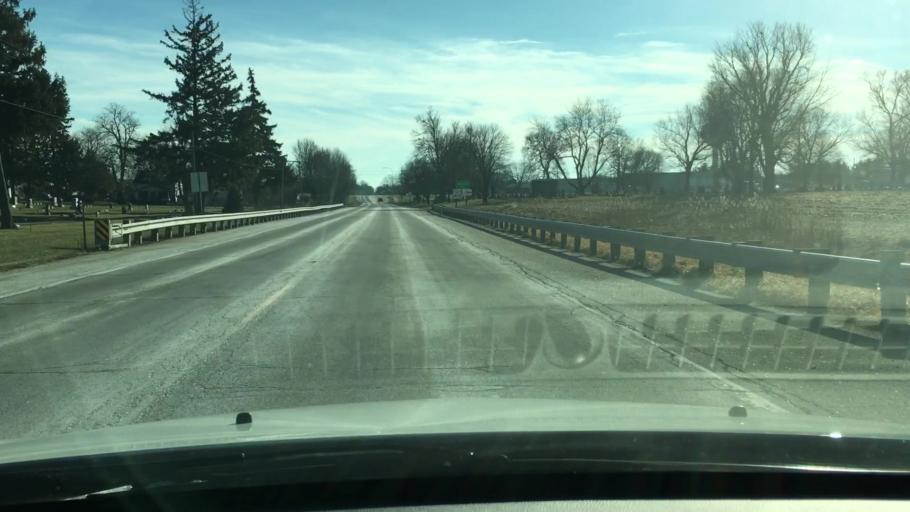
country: US
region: Illinois
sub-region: LaSalle County
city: Mendota
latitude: 41.5658
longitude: -89.1280
